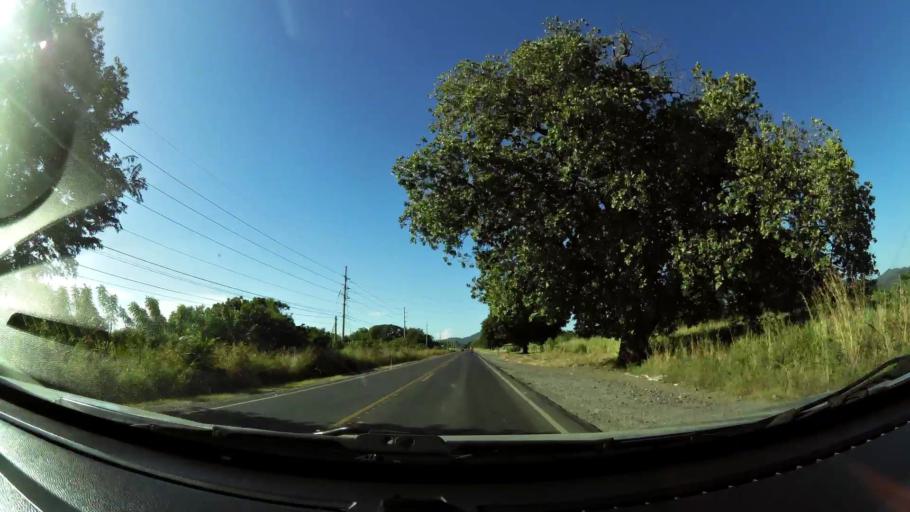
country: CR
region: Guanacaste
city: Belen
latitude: 10.4284
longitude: -85.5696
